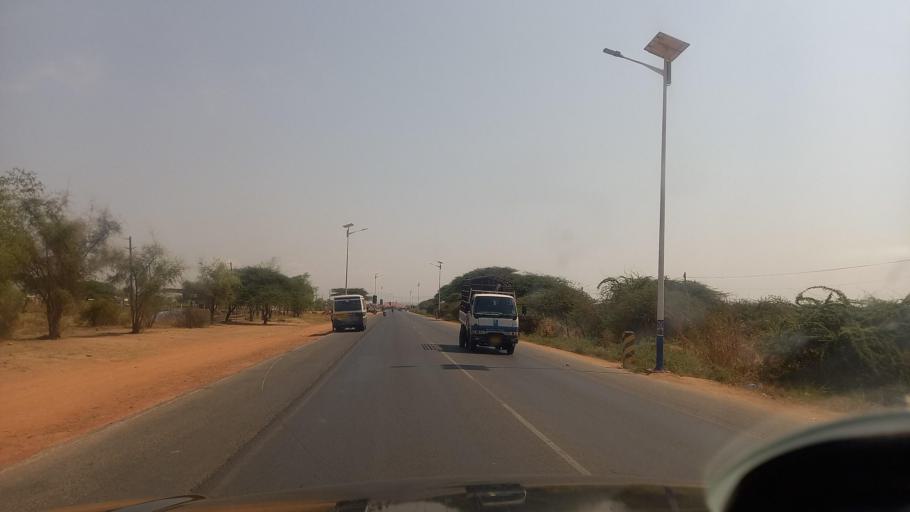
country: TZ
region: Dodoma
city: Kisasa
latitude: -6.1491
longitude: 35.8101
